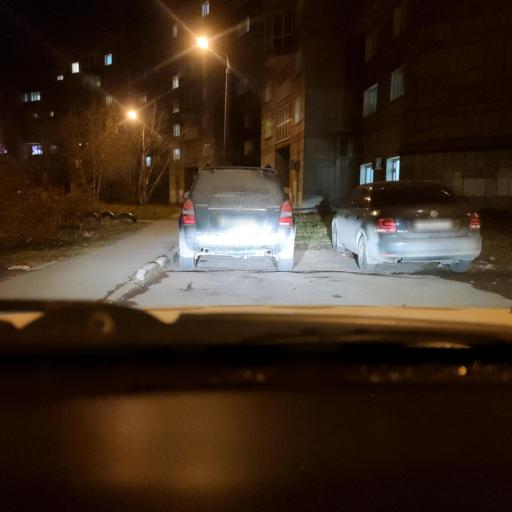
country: RU
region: Perm
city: Perm
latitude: 57.9865
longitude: 56.1894
